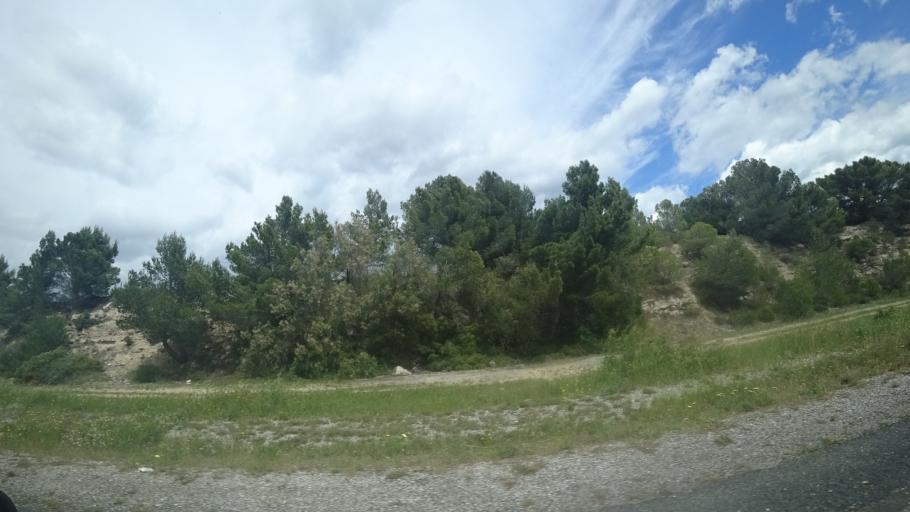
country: FR
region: Languedoc-Roussillon
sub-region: Departement de l'Aude
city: Leucate
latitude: 42.9170
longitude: 3.0211
